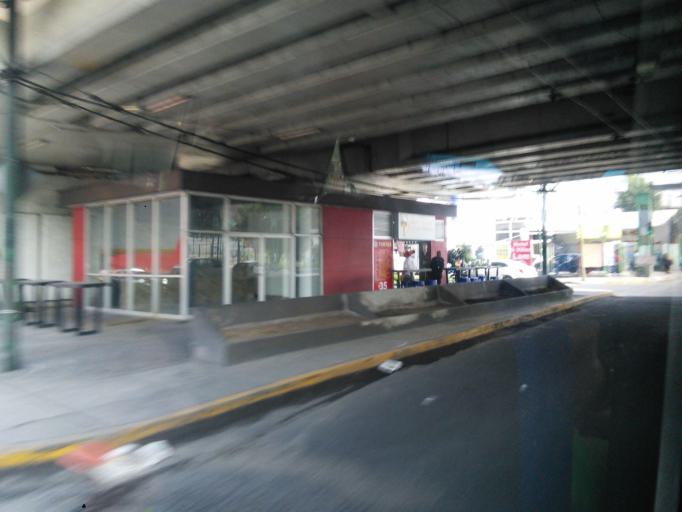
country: MX
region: Mexico City
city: Cuauhtemoc
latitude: 19.4650
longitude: -99.1375
